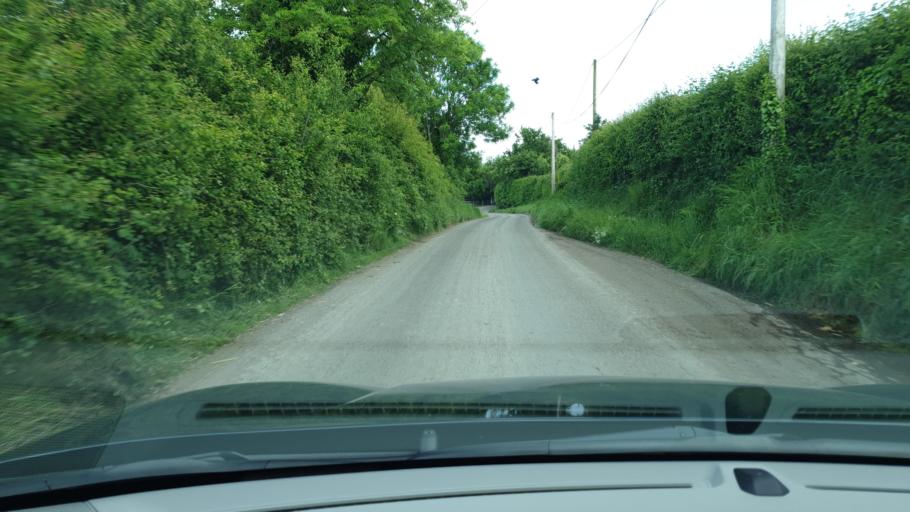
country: IE
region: Leinster
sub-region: An Mhi
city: Ratoath
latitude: 53.5677
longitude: -6.4530
